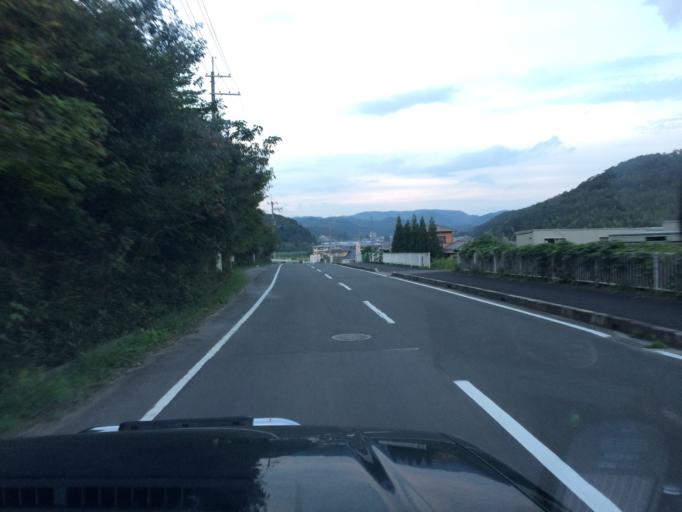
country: JP
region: Kyoto
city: Kameoka
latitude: 35.0925
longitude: 135.4756
